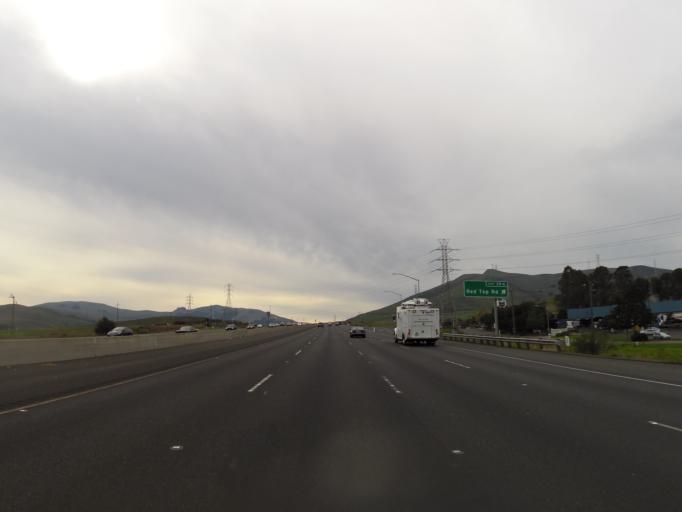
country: US
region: California
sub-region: Solano County
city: Green Valley
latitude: 38.2044
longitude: -122.1550
